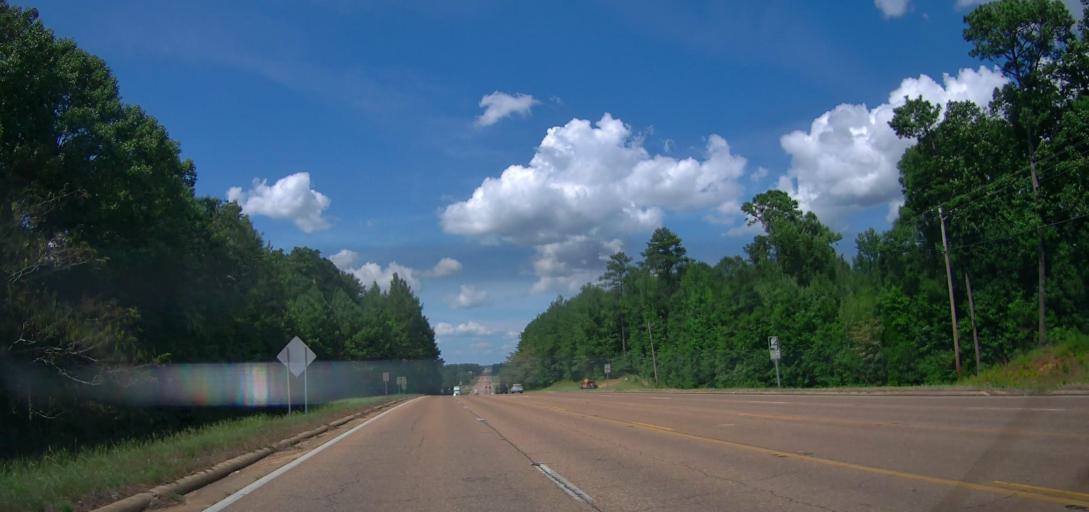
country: US
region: Mississippi
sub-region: Lowndes County
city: Columbus
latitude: 33.5653
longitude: -88.4327
